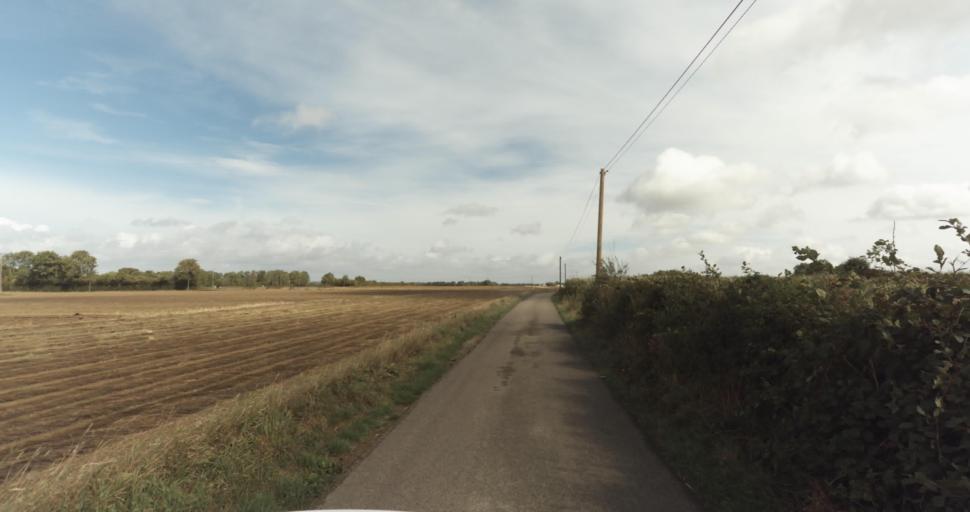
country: FR
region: Lower Normandy
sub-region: Departement de l'Orne
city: Gace
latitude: 48.8229
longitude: 0.3969
